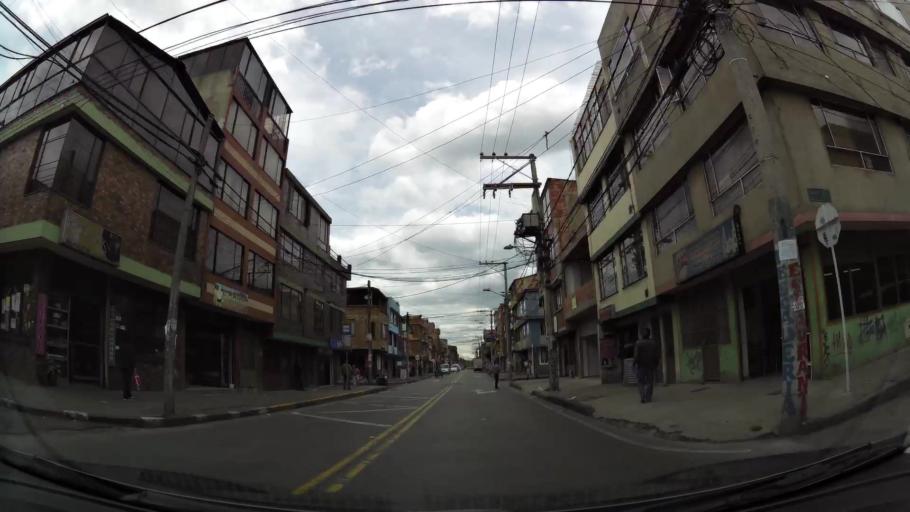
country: CO
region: Cundinamarca
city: Funza
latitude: 4.7050
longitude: -74.1248
